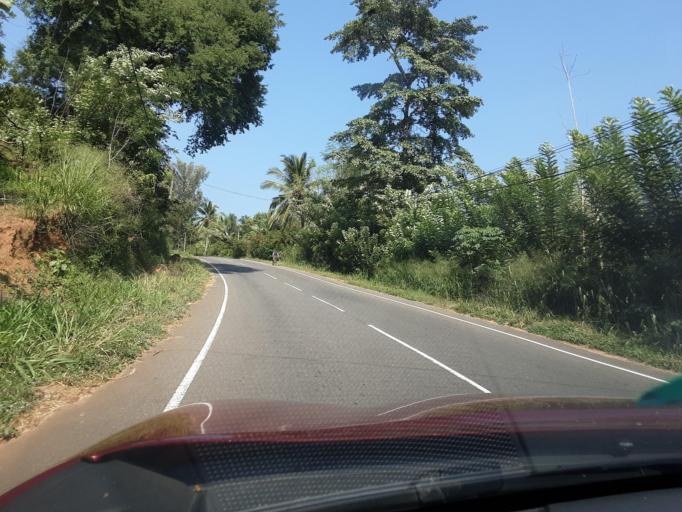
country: LK
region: Uva
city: Badulla
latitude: 7.1827
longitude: 81.0459
